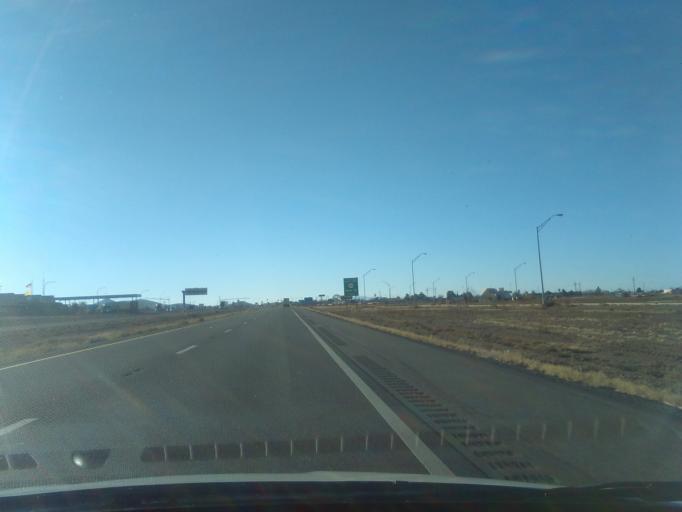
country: US
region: New Mexico
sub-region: Hidalgo County
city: Lordsburg
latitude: 32.3414
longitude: -108.6949
